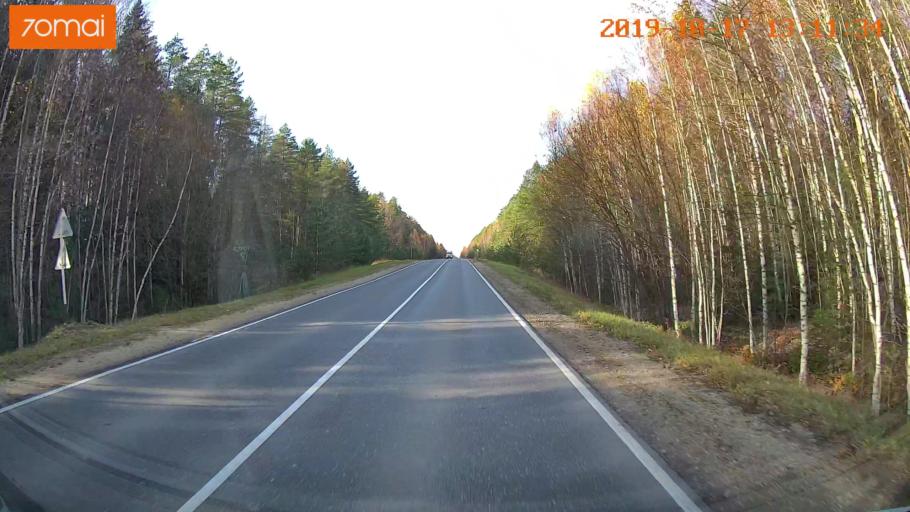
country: RU
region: Rjazan
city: Syntul
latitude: 55.0288
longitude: 41.2323
